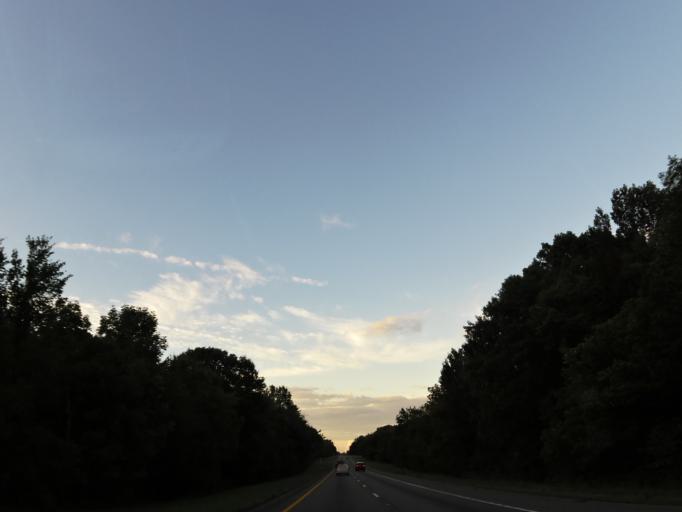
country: US
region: Tennessee
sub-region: McMinn County
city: Athens
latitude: 35.4360
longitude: -84.6791
